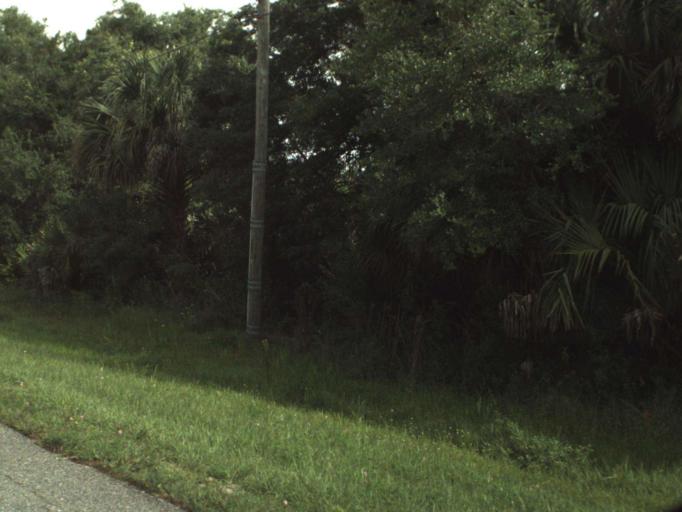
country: US
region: Florida
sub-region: Seminole County
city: Geneva
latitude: 28.7677
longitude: -81.1533
